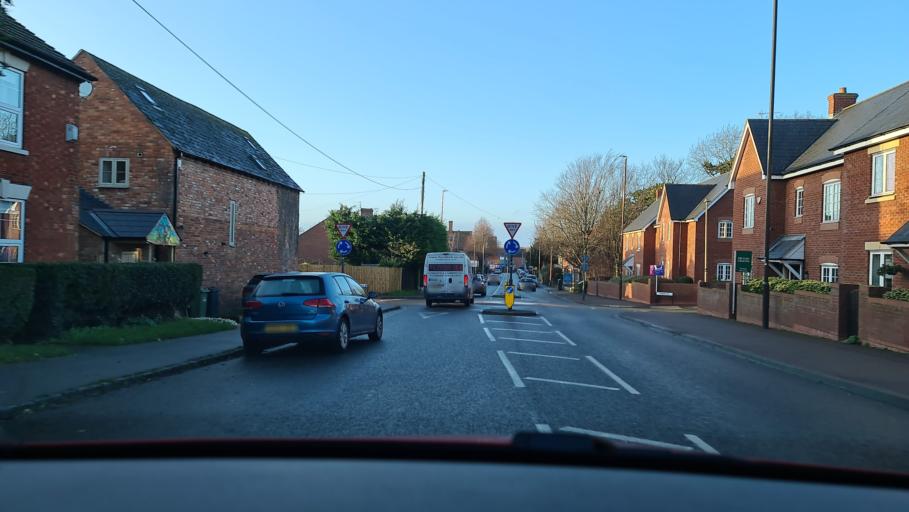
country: GB
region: England
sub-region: Milton Keynes
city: Stony Stratford
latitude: 52.0539
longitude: -0.8472
